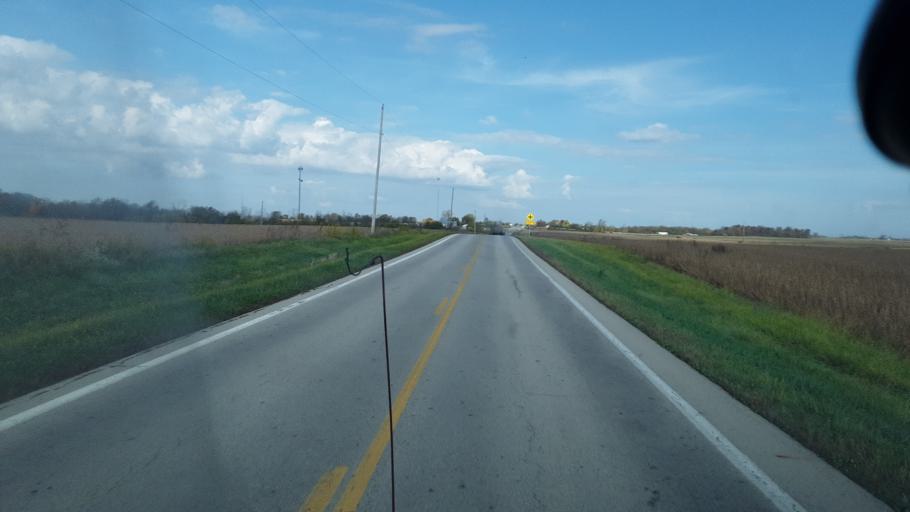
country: US
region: Ohio
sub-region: Clinton County
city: Sabina
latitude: 39.5474
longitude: -83.7131
